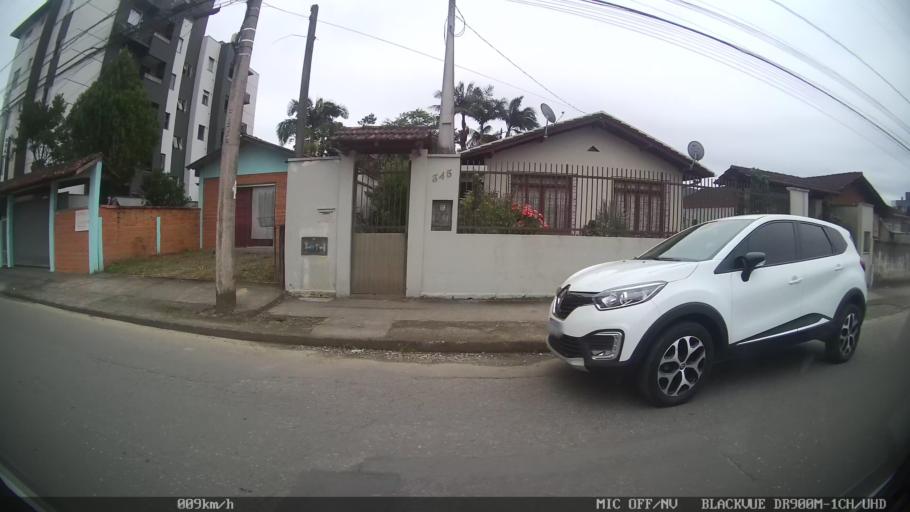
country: BR
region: Santa Catarina
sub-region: Joinville
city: Joinville
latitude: -26.2826
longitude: -48.9070
